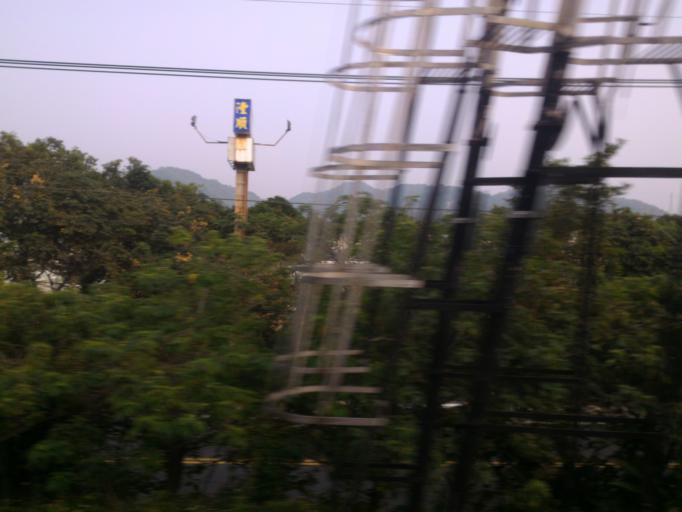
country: TW
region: Taiwan
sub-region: Taoyuan
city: Taoyuan
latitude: 24.9681
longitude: 121.3395
